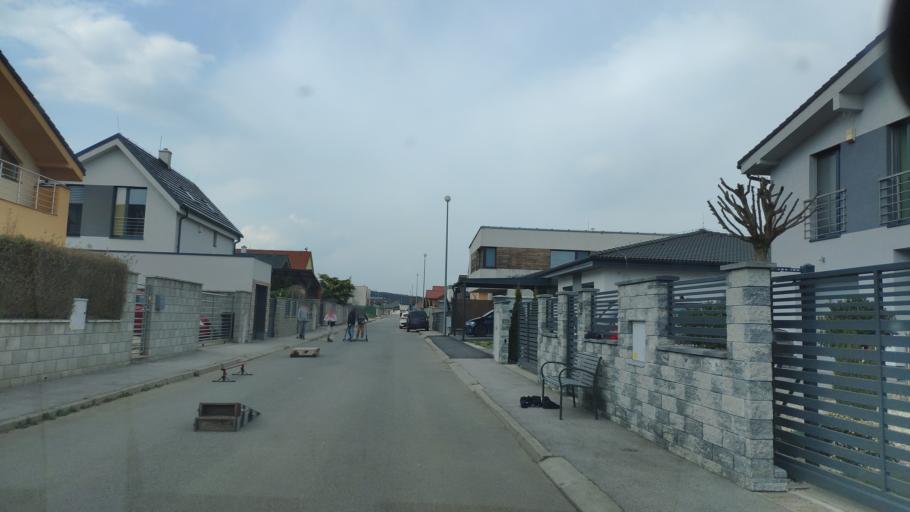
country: SK
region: Kosicky
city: Kosice
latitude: 48.6774
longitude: 21.3133
